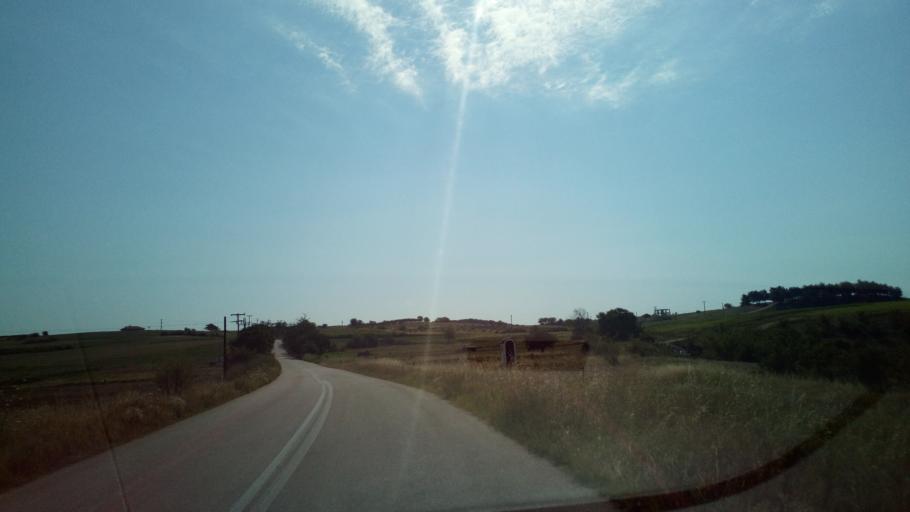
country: GR
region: Central Macedonia
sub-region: Nomos Thessalonikis
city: Askos
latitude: 40.7375
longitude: 23.3767
